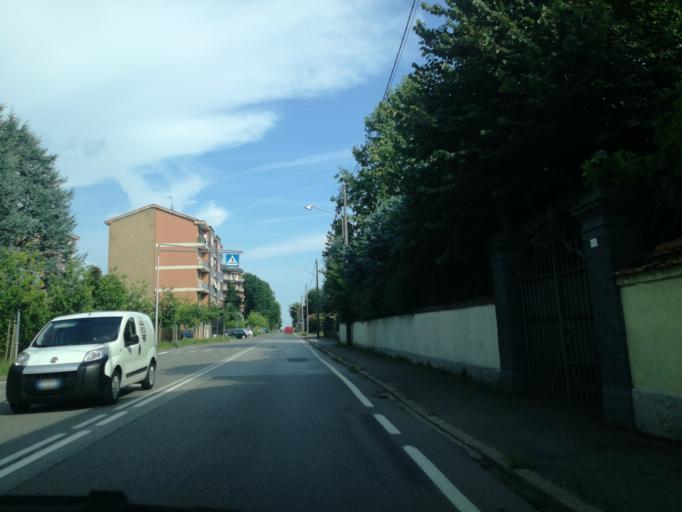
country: IT
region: Lombardy
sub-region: Provincia di Lecco
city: Cernusco Lombardone
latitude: 45.6924
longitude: 9.4032
